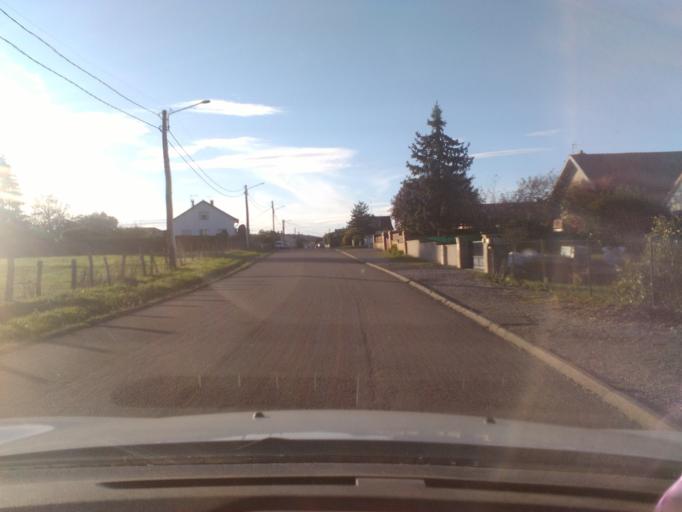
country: FR
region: Lorraine
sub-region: Departement des Vosges
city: Vincey
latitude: 48.3367
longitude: 6.3375
